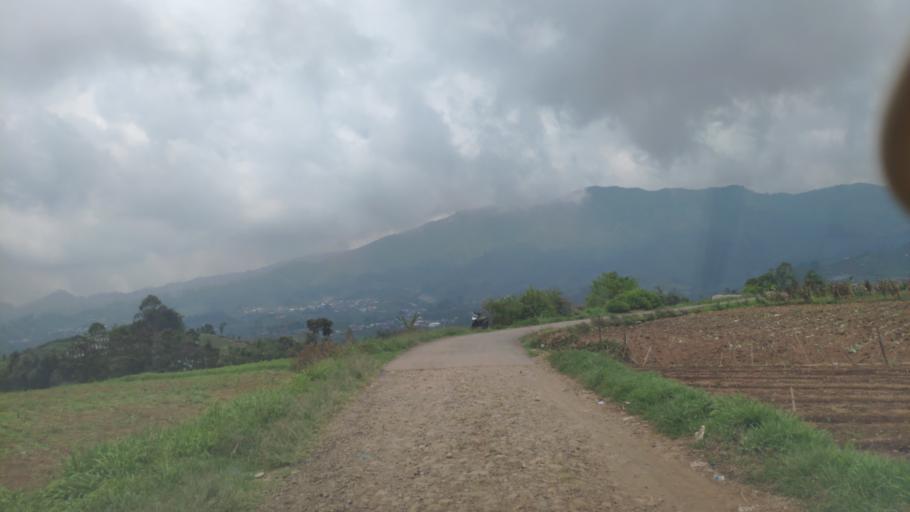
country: ID
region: Central Java
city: Wonosobo
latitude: -7.2167
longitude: 109.7873
